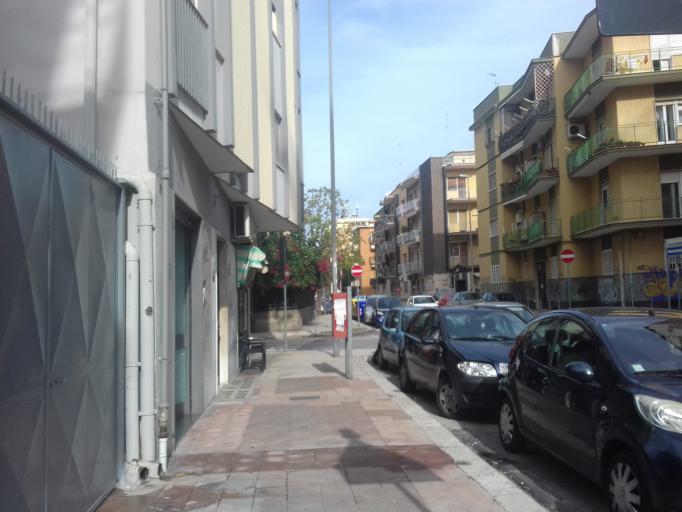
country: IT
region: Apulia
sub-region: Provincia di Bari
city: Bari
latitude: 41.1085
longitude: 16.8758
